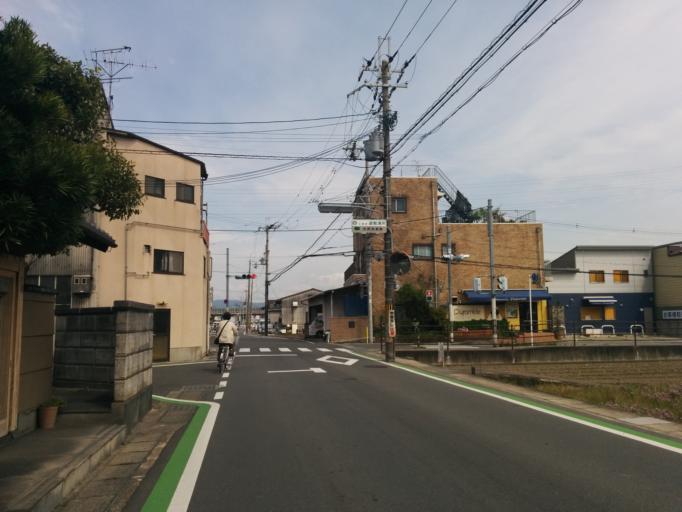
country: JP
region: Kyoto
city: Muko
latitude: 34.9428
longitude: 135.7117
